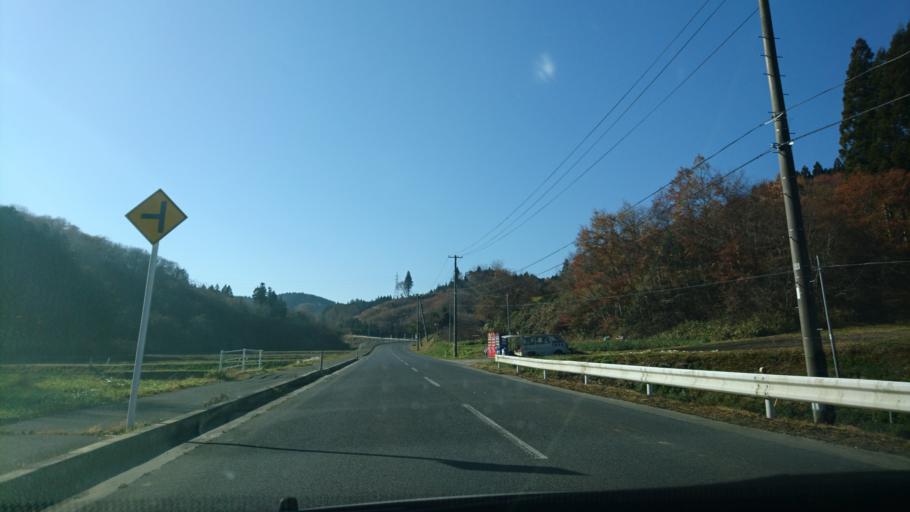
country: JP
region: Iwate
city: Ichinoseki
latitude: 38.9024
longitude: 141.4220
